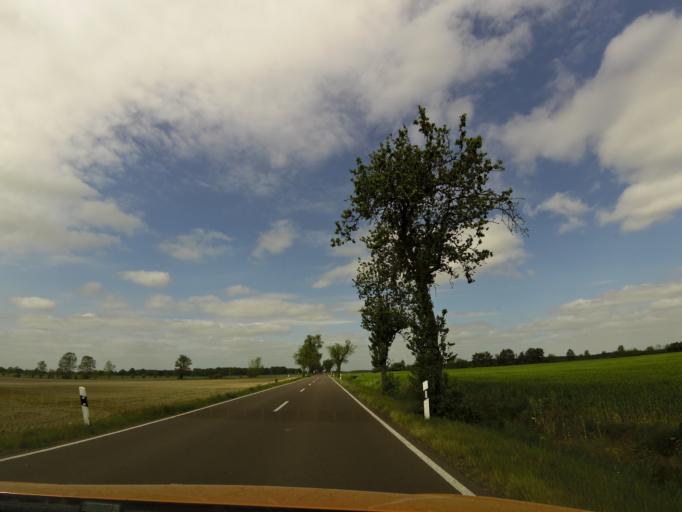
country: DE
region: Saxony-Anhalt
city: Loburg
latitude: 52.1088
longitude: 12.1597
